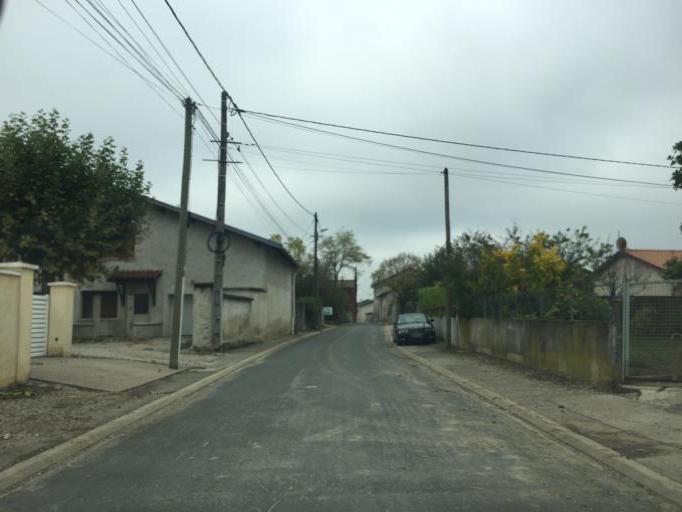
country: FR
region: Rhone-Alpes
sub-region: Departement de l'Ain
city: Nievroz
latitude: 45.8237
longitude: 5.0578
